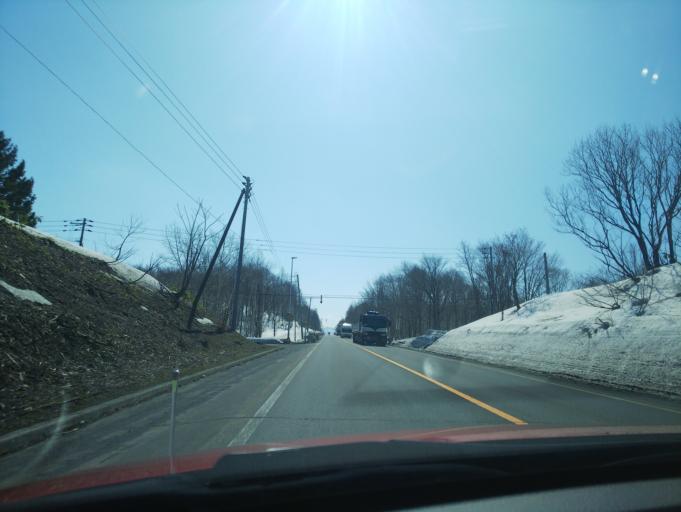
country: JP
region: Hokkaido
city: Nayoro
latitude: 44.6444
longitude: 142.2667
